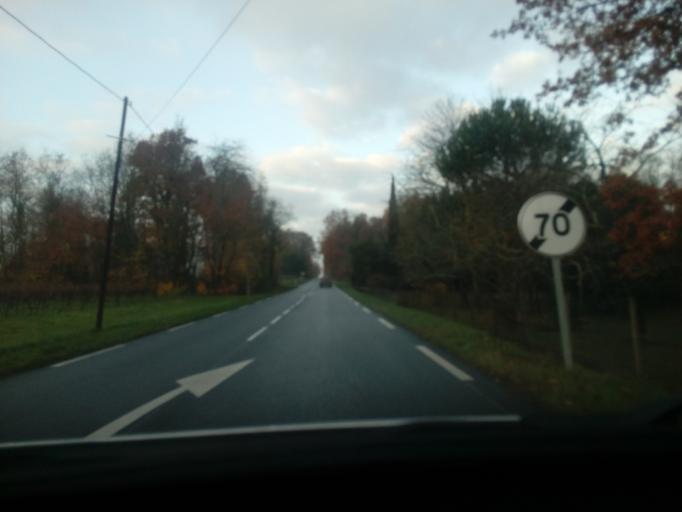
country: FR
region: Poitou-Charentes
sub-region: Departement de la Charente-Maritime
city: Jonzac
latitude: 45.4428
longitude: -0.3585
